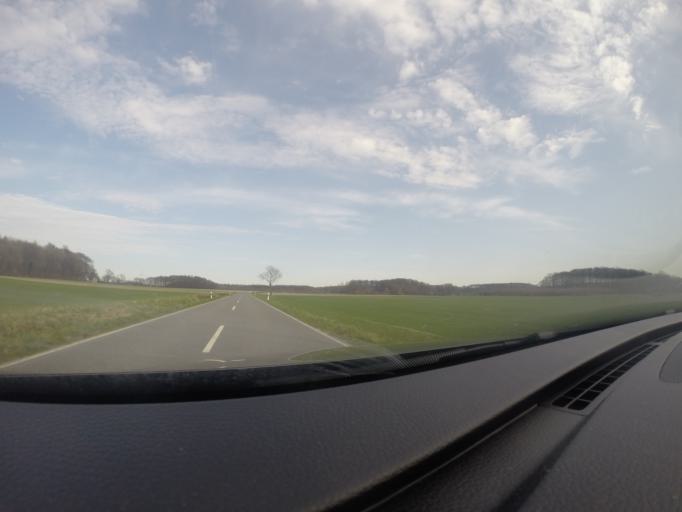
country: DE
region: North Rhine-Westphalia
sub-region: Regierungsbezirk Munster
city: Legden
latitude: 52.0550
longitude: 7.1708
